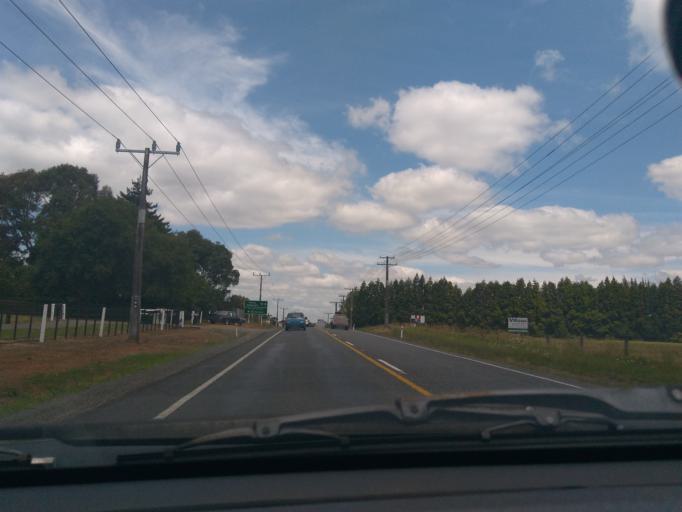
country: NZ
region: Northland
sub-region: Far North District
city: Kerikeri
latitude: -35.2041
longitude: 173.9148
